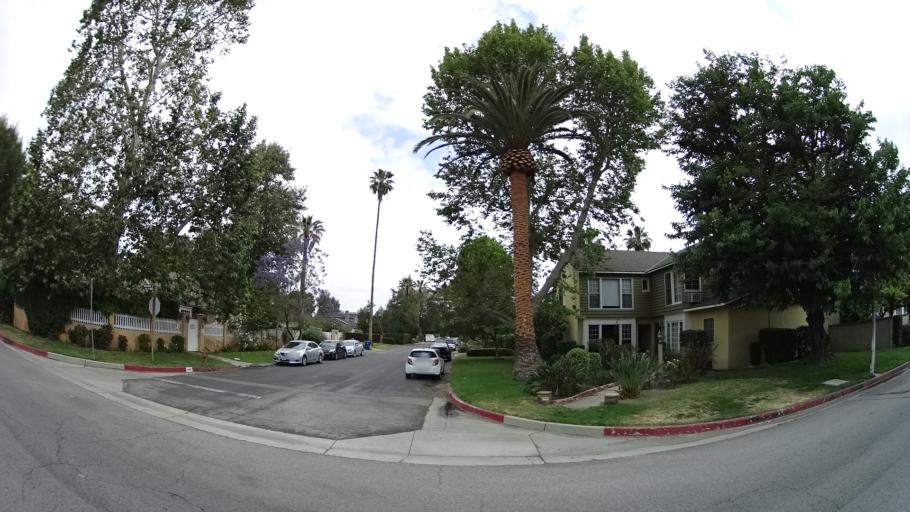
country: US
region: California
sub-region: Los Angeles County
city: North Hollywood
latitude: 34.1504
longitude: -118.3898
